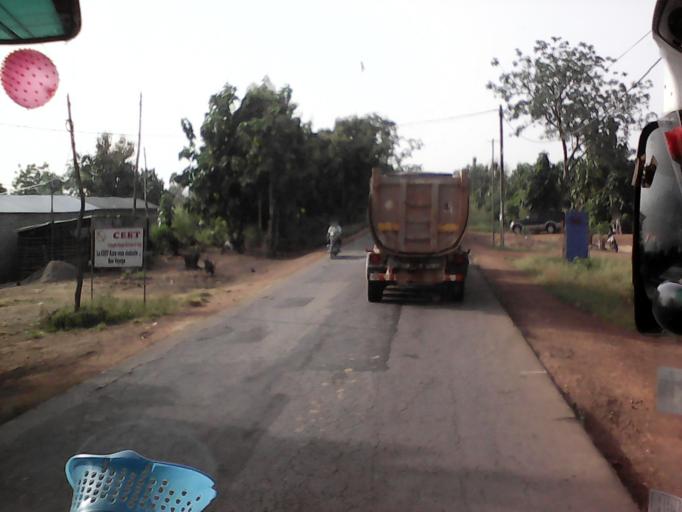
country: TG
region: Kara
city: Kara
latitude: 9.5038
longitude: 1.2090
